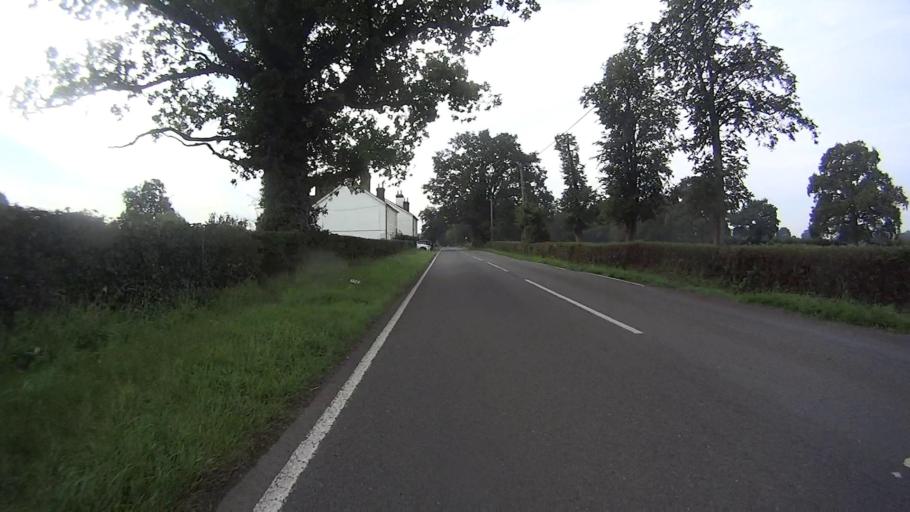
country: GB
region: England
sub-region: West Sussex
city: Copthorne
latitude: 51.1498
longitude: -0.1106
